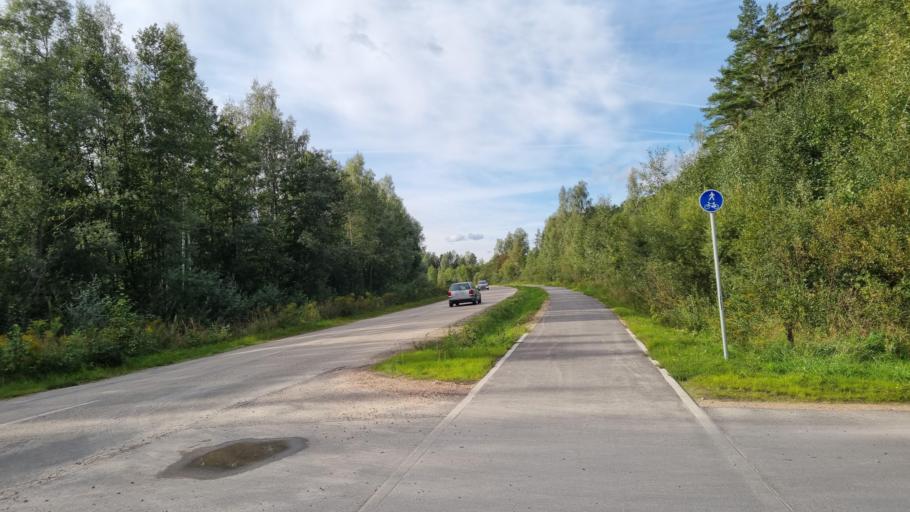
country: LV
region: Lecava
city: Iecava
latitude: 56.6957
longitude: 24.0862
